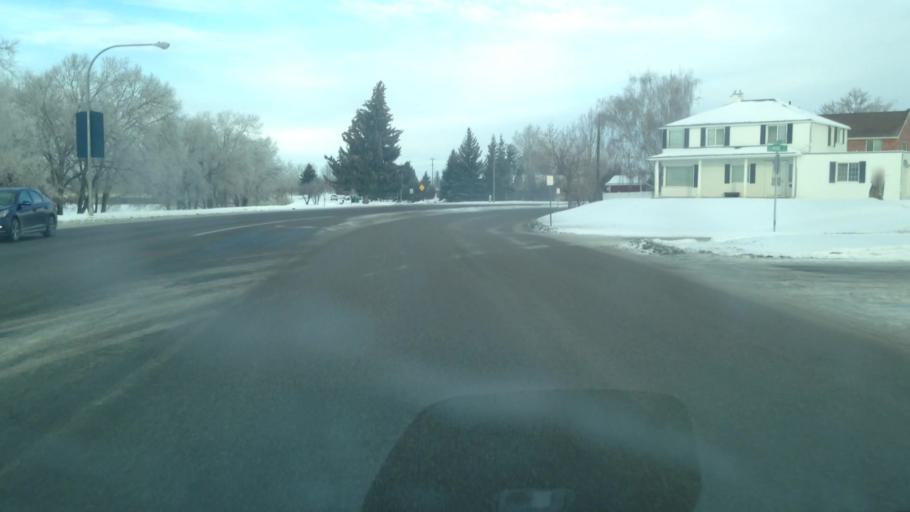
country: US
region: Idaho
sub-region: Bonneville County
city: Idaho Falls
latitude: 43.5043
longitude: -112.0460
